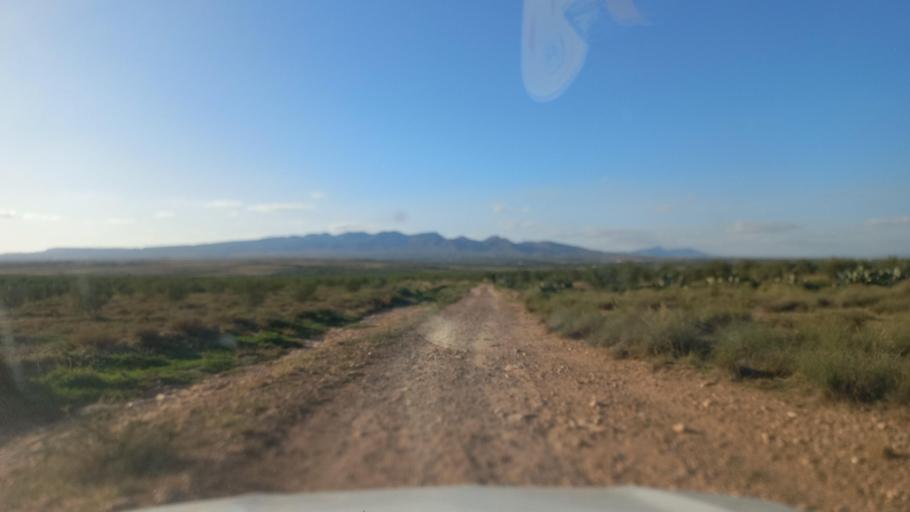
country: TN
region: Al Qasrayn
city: Sbiba
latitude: 35.3879
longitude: 9.1539
